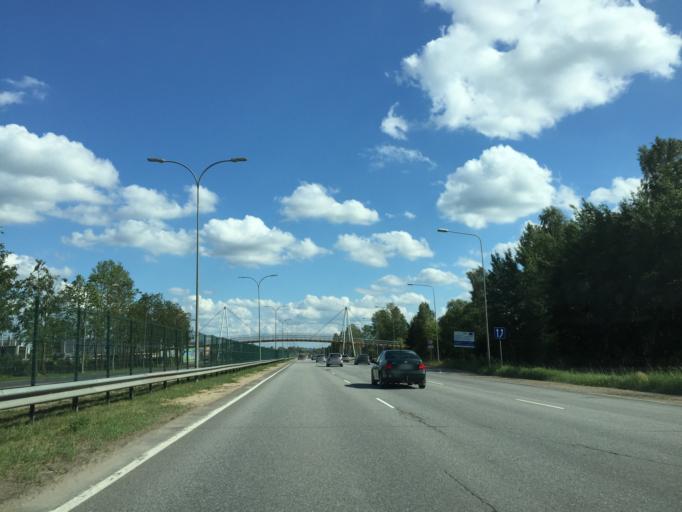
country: LV
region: Marupe
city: Marupe
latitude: 56.9421
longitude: 23.9975
